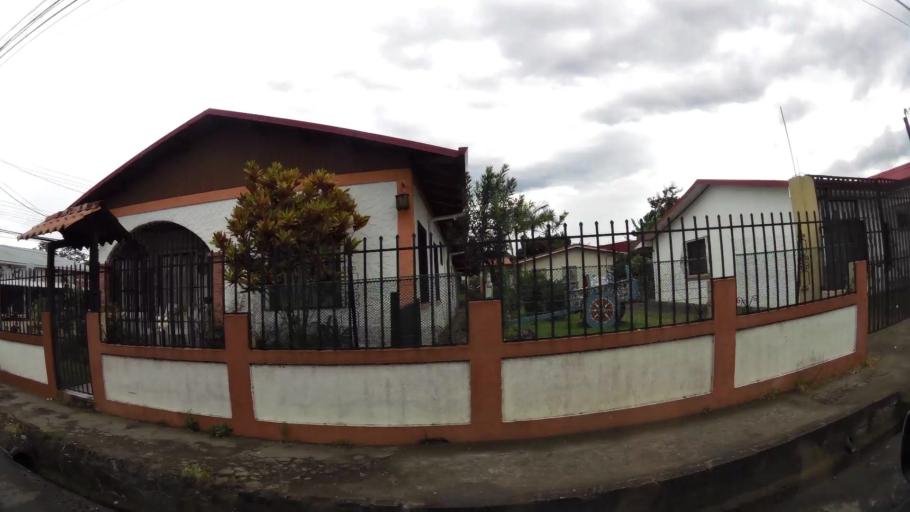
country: CR
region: Heredia
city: San Pablo
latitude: 9.9830
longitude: -84.0939
